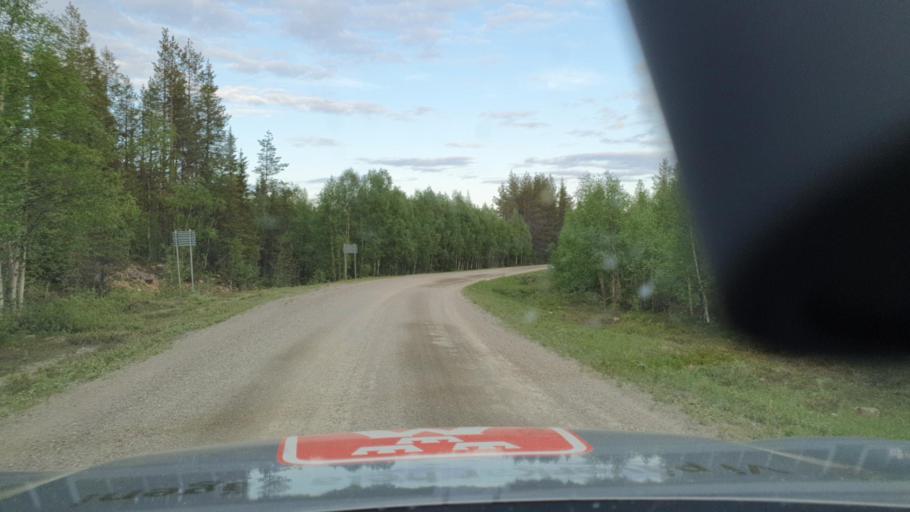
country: SE
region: Norrbotten
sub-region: Bodens Kommun
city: Boden
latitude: 66.6009
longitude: 21.3671
